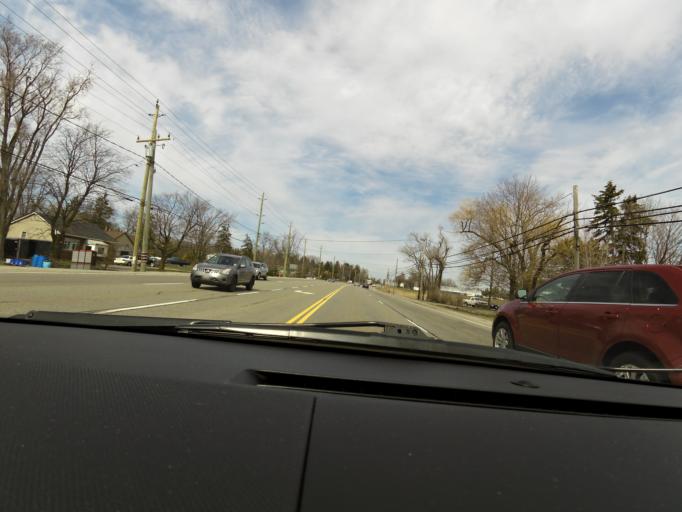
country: CA
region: Ontario
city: Ancaster
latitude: 43.1685
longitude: -79.9085
